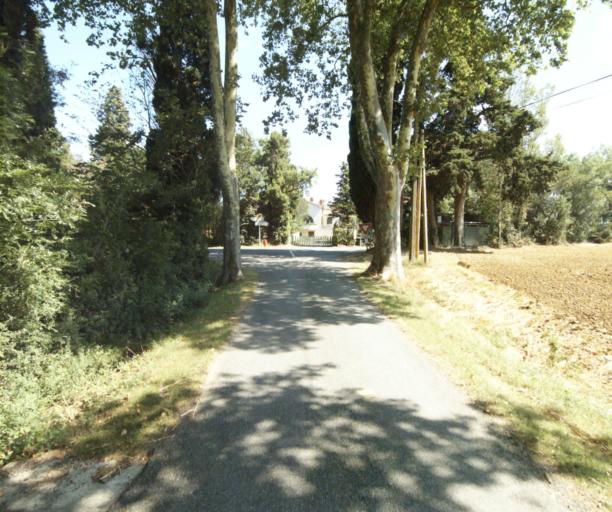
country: FR
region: Midi-Pyrenees
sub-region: Departement de la Haute-Garonne
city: Auriac-sur-Vendinelle
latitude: 43.4680
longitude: 1.7959
